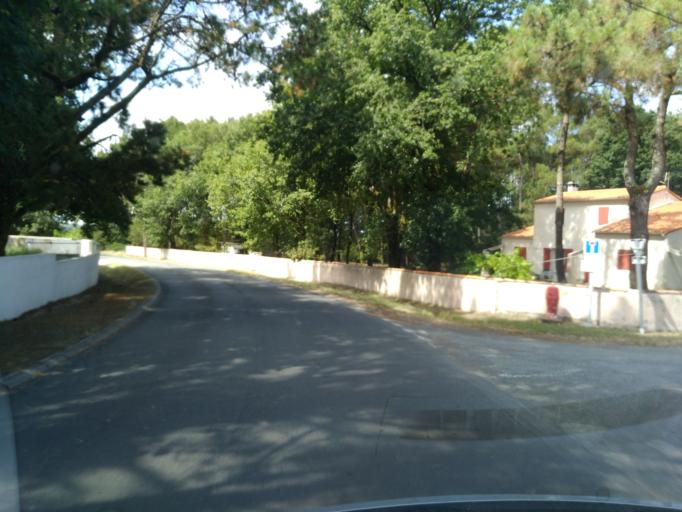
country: FR
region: Poitou-Charentes
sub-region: Departement de la Charente-Maritime
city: Breuillet
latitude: 45.6863
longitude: -1.0767
